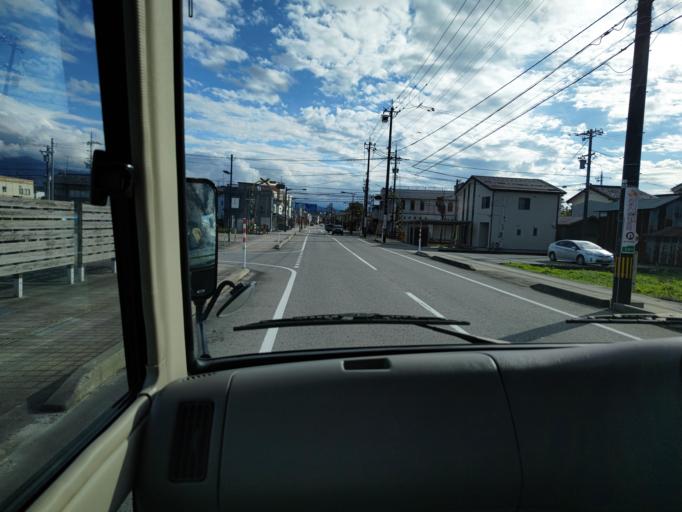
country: JP
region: Toyama
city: Nyuzen
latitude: 36.8747
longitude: 137.4469
